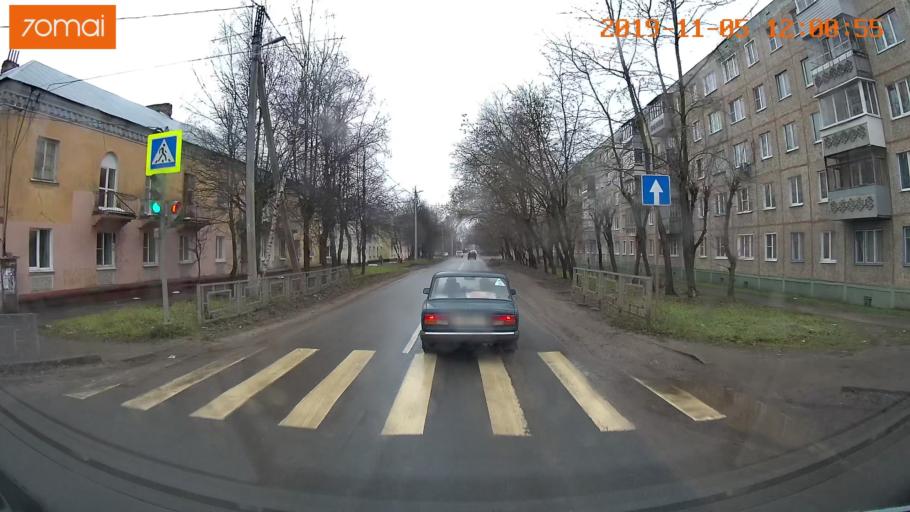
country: RU
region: Ivanovo
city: Kokhma
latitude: 56.9754
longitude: 41.0476
